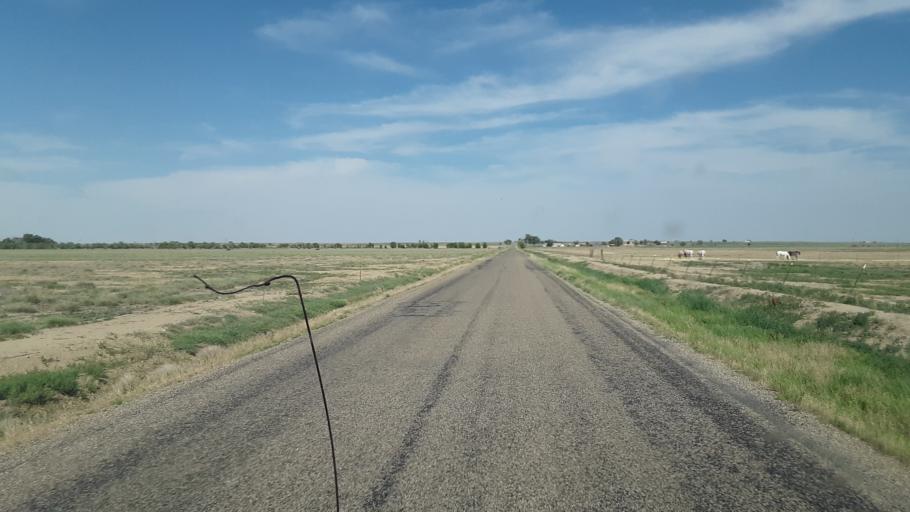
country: US
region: Colorado
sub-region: Otero County
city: Fowler
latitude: 38.1631
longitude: -103.9029
